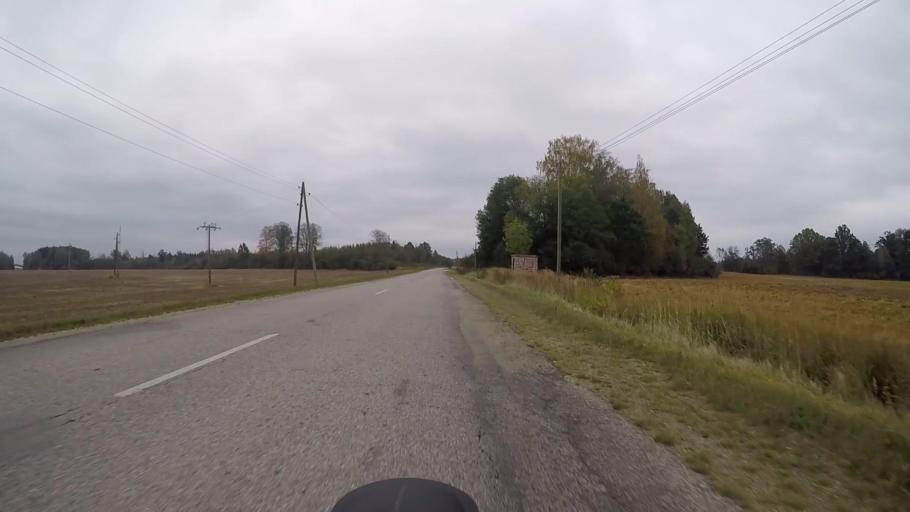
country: LV
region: Seja
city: Loja
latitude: 57.2748
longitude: 24.5752
